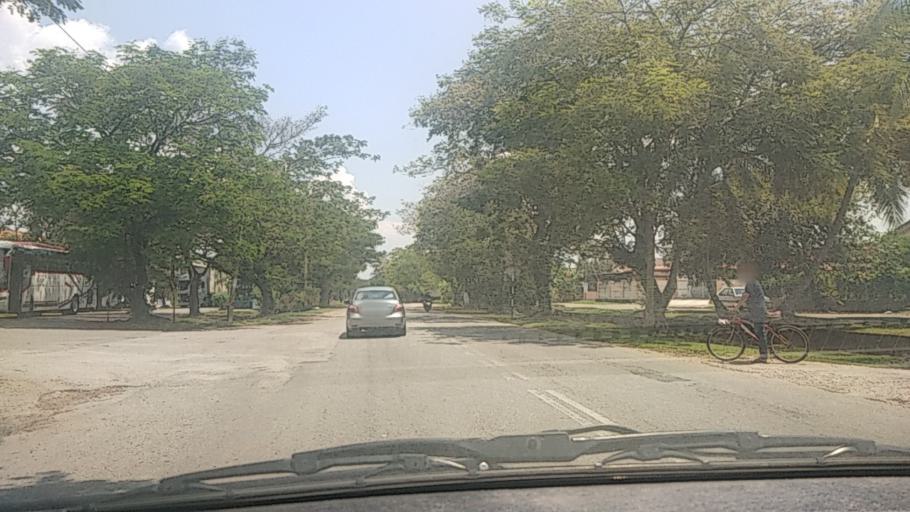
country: MY
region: Kedah
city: Sungai Petani
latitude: 5.6458
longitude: 100.5263
